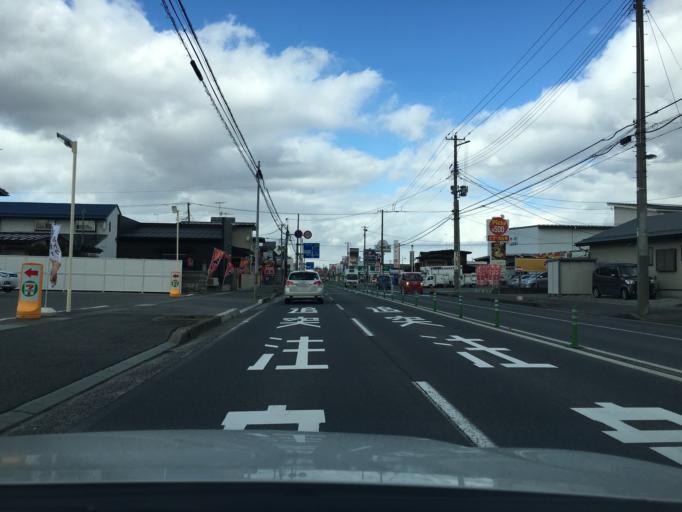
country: JP
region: Yamagata
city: Yamagata-shi
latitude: 38.2353
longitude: 140.3059
